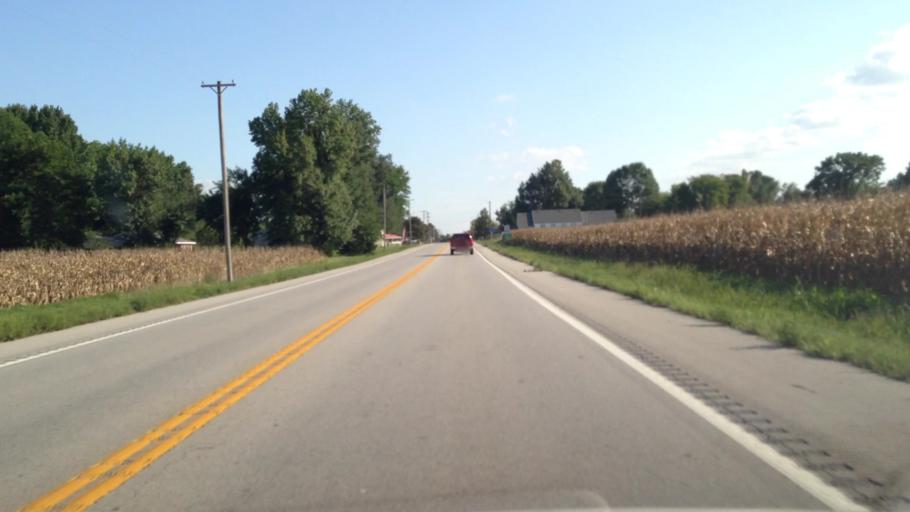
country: US
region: Missouri
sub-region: Jasper County
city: Carl Junction
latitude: 37.2780
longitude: -94.6010
